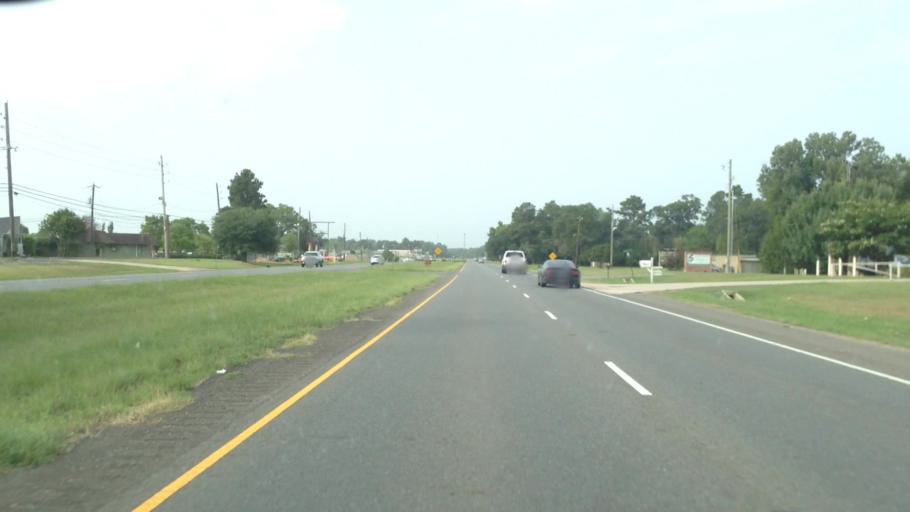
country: US
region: Louisiana
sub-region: De Soto Parish
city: Stonewall
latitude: 32.3724
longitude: -93.8231
